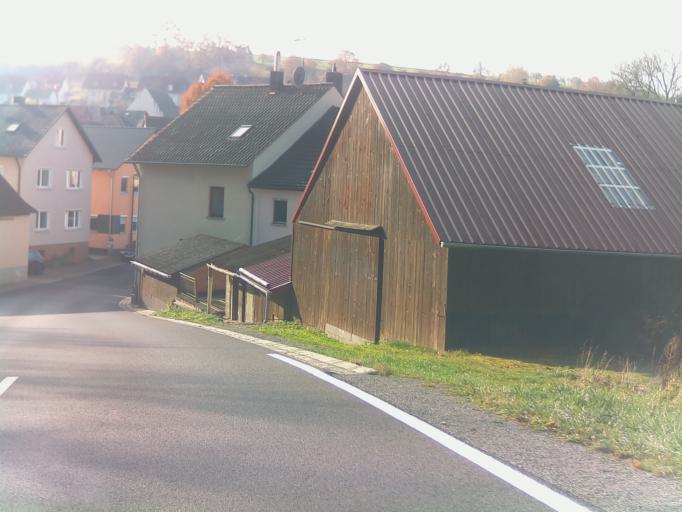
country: DE
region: Bavaria
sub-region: Regierungsbezirk Unterfranken
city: Burkardroth
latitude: 50.2474
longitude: 10.0114
